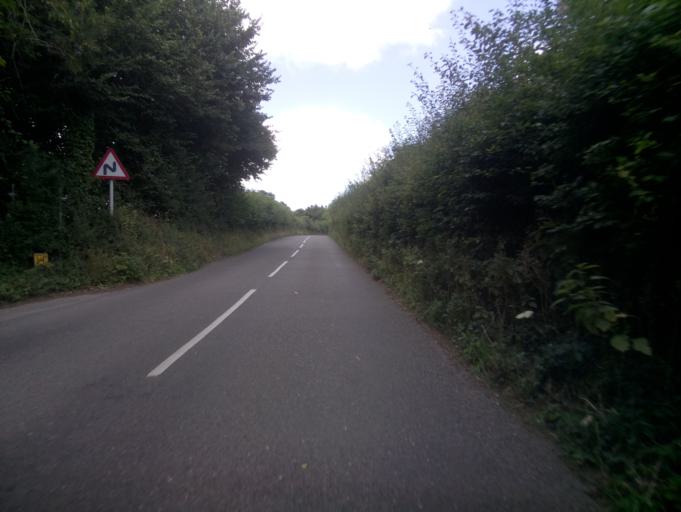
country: GB
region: England
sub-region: Oxfordshire
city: Faringdon
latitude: 51.6311
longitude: -1.5862
